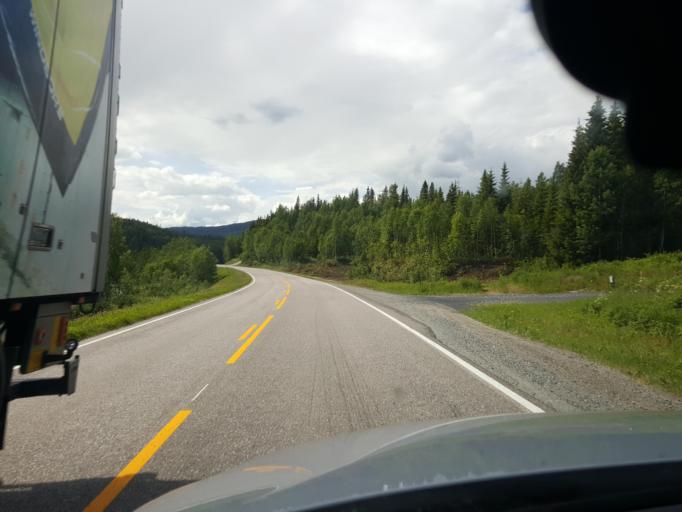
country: NO
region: Nordland
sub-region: Rana
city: Mo i Rana
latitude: 66.4068
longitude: 14.4976
